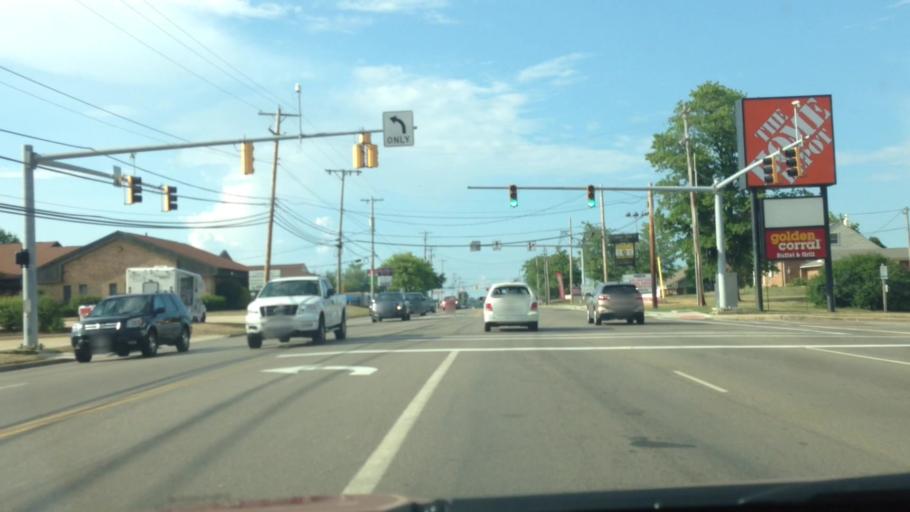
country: US
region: Ohio
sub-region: Summit County
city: Portage Lakes
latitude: 40.9951
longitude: -81.4923
